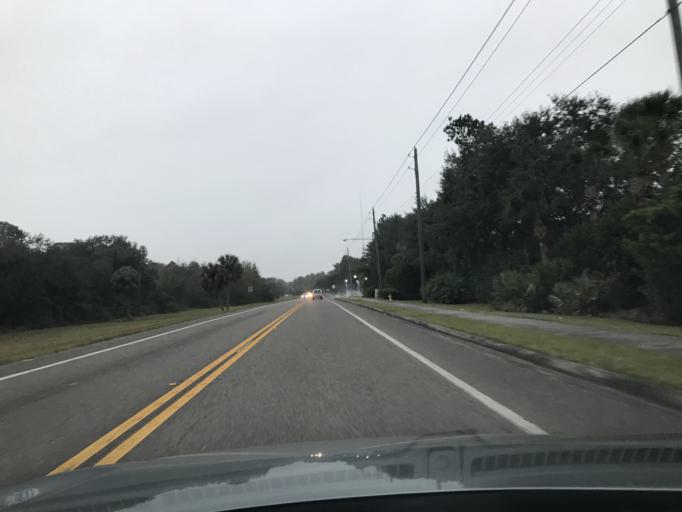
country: US
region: Florida
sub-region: Hillsborough County
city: Westchase
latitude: 28.0563
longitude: -82.6359
